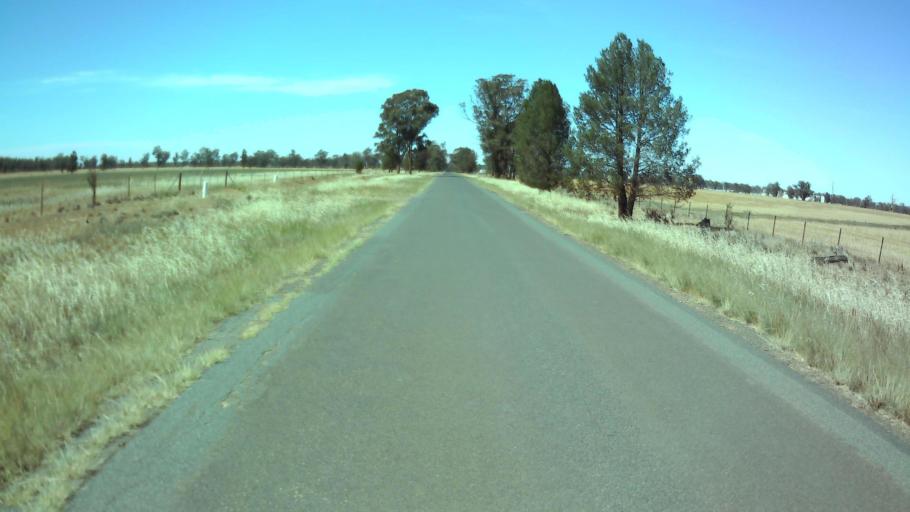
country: AU
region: New South Wales
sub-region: Weddin
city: Grenfell
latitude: -34.1043
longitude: 147.8870
